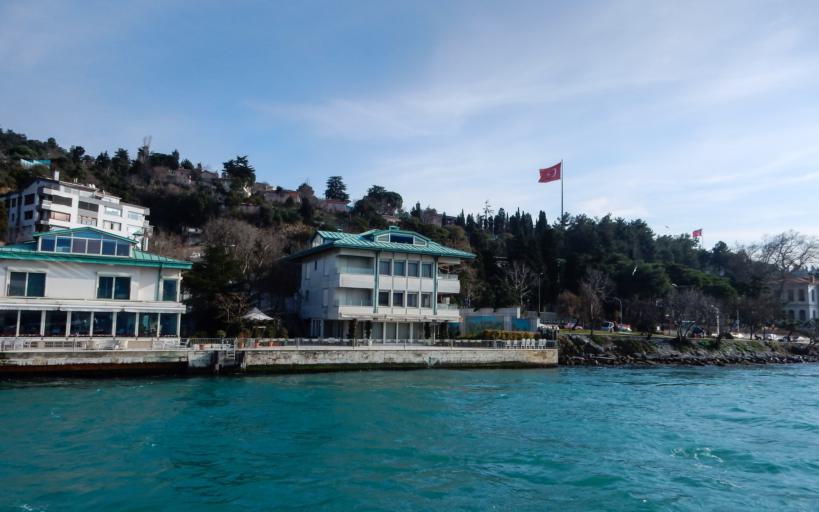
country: TR
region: Istanbul
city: UEskuedar
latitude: 41.0614
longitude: 29.0518
